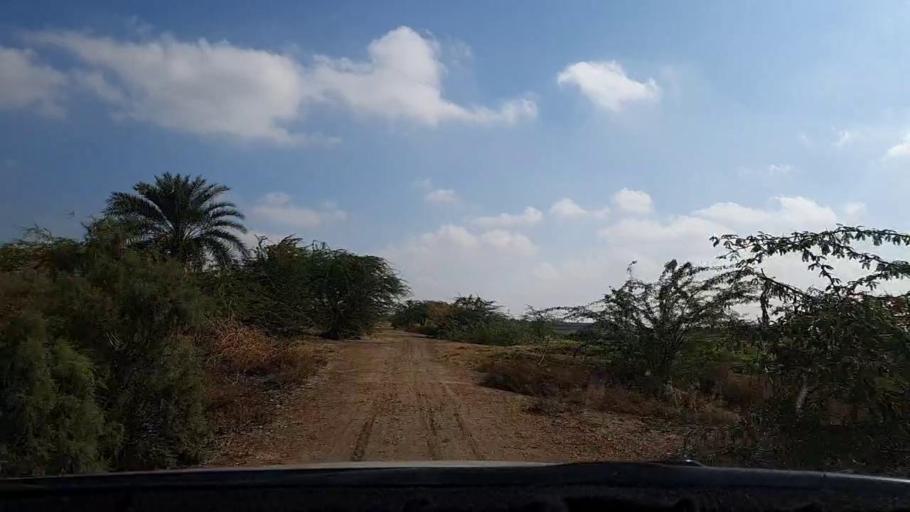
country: PK
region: Sindh
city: Pithoro
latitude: 25.7226
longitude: 69.2934
